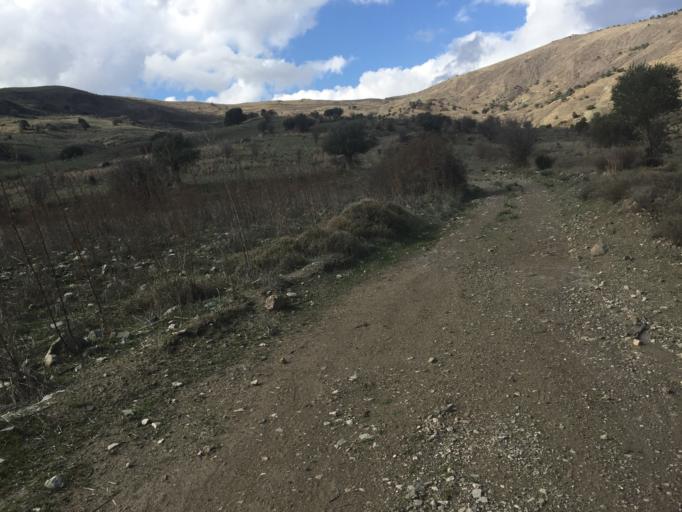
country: CY
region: Limassol
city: Pachna
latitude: 34.8704
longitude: 32.6663
